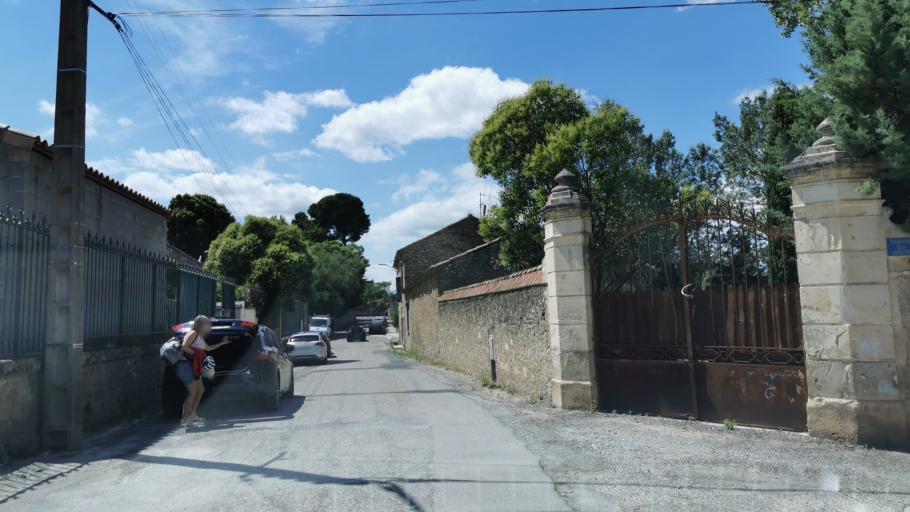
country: FR
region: Languedoc-Roussillon
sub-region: Departement de l'Aude
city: Saint-Marcel-sur-Aude
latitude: 43.2443
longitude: 2.9231
